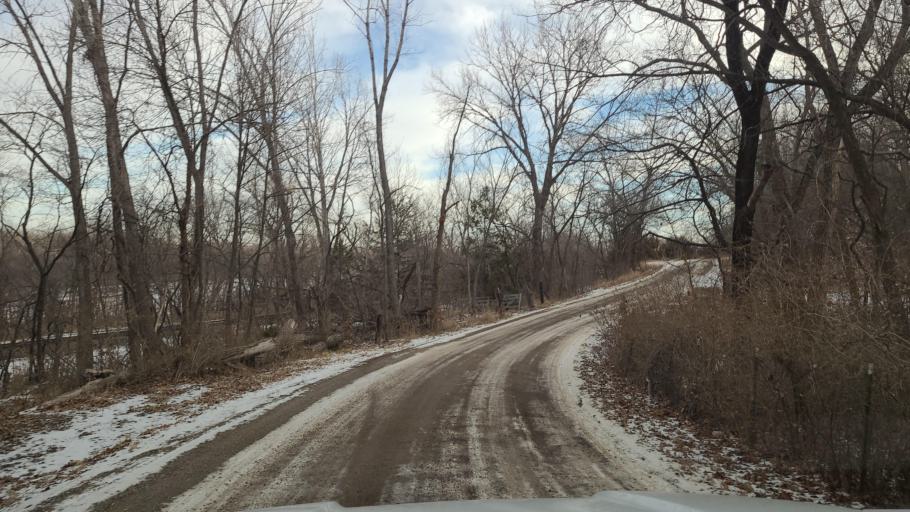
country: US
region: Kansas
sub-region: Shawnee County
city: Topeka
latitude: 39.0545
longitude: -95.4822
